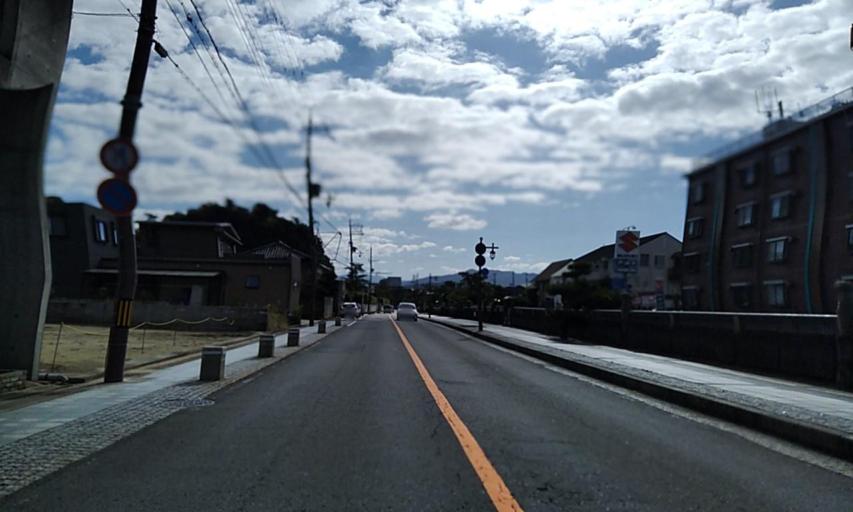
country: JP
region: Wakayama
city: Minato
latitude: 34.1889
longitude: 135.1686
